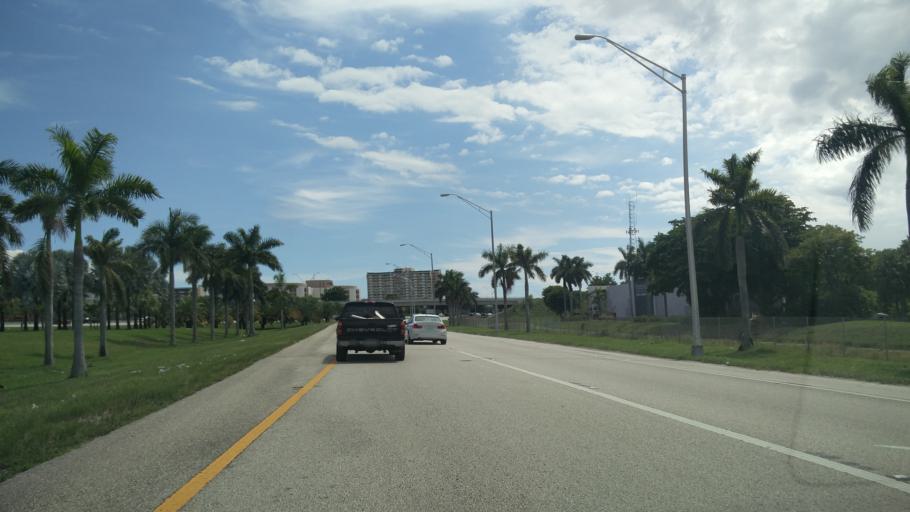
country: US
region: Florida
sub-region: Broward County
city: Pompano Beach
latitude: 26.2296
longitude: -80.1380
